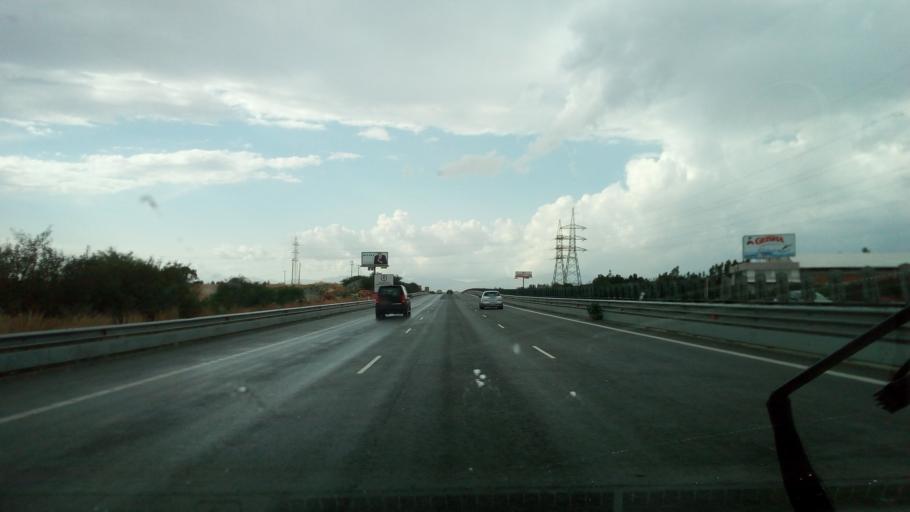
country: CY
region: Lefkosia
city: Geri
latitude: 35.0901
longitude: 33.3747
